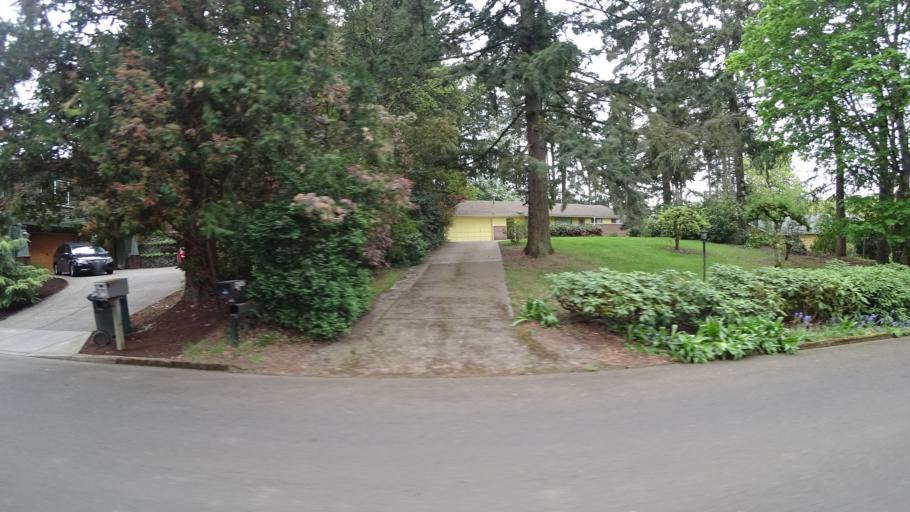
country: US
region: Oregon
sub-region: Washington County
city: Beaverton
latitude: 45.4629
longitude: -122.8242
